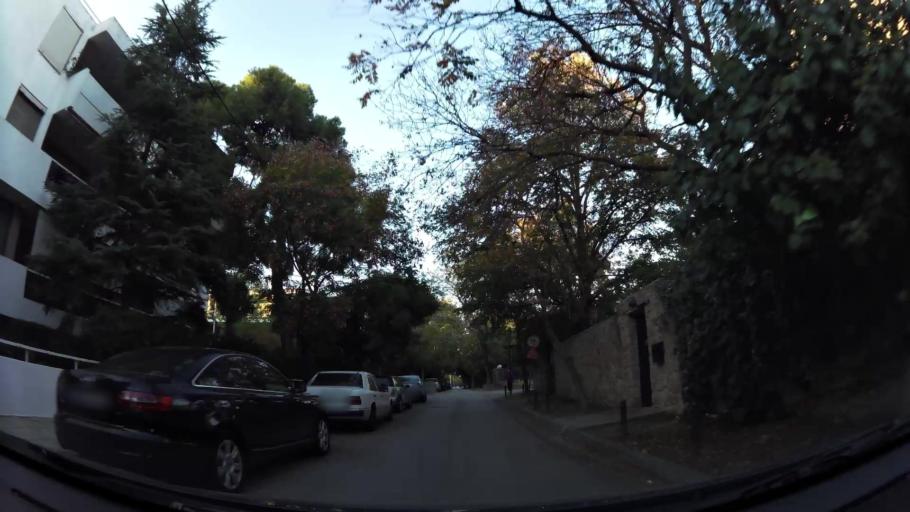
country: GR
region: Attica
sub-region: Nomarchia Athinas
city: Kifisia
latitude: 38.0820
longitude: 23.8160
